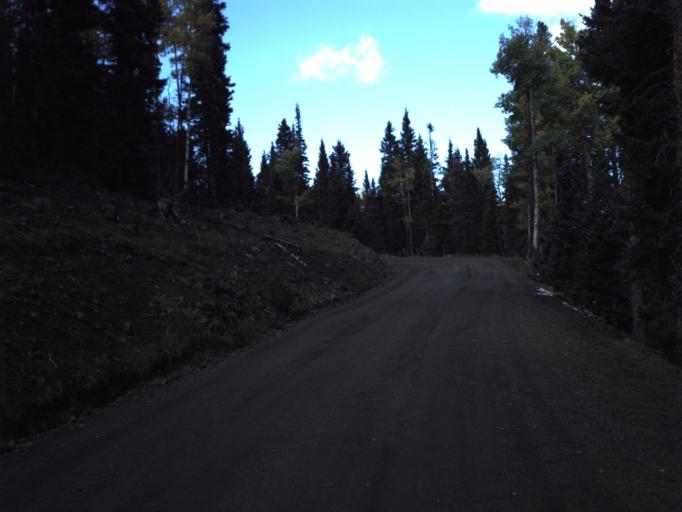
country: US
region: Utah
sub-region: Piute County
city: Junction
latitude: 38.2392
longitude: -112.3686
